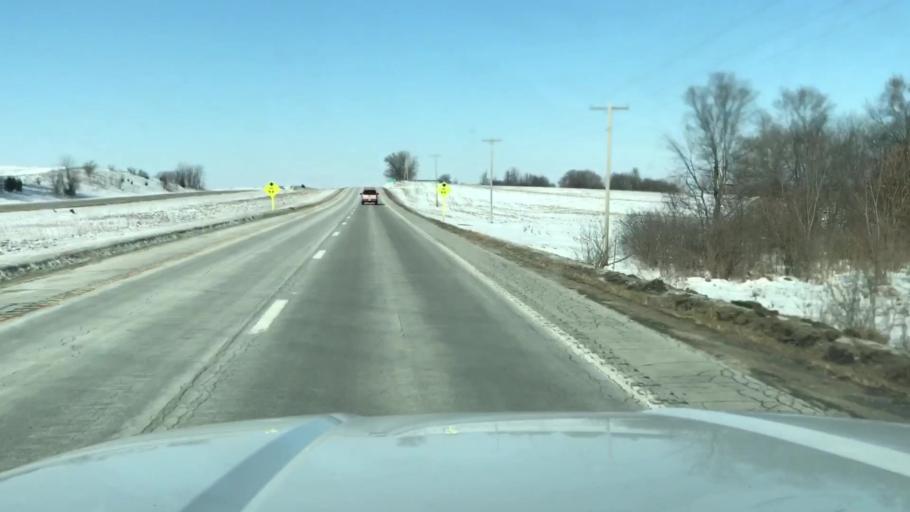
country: US
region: Missouri
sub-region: Andrew County
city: Savannah
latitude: 39.9669
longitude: -94.8668
